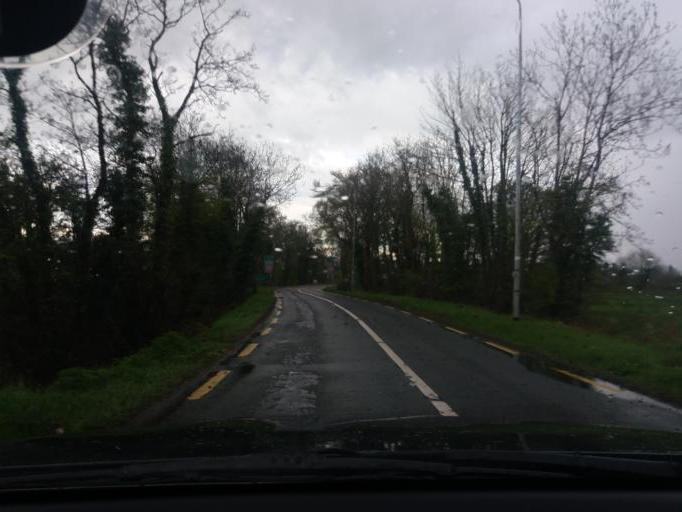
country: IE
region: Ulster
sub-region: An Cabhan
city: Ballyconnell
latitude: 54.1253
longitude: -7.6803
